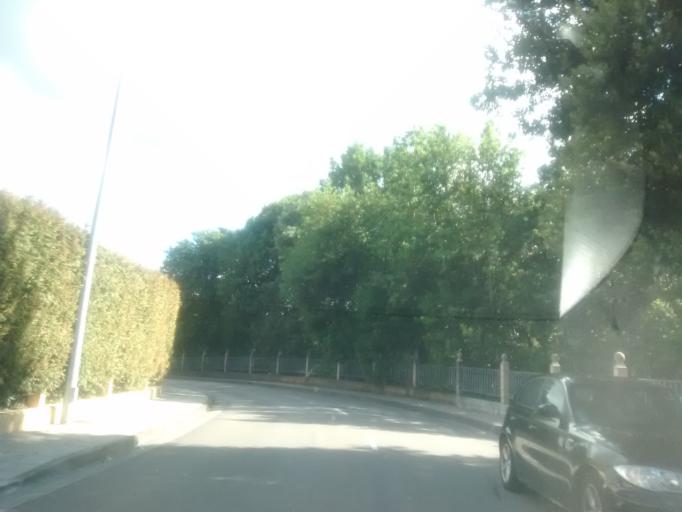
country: ES
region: Cantabria
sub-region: Provincia de Cantabria
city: Lierganes
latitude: 43.3799
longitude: -3.7369
